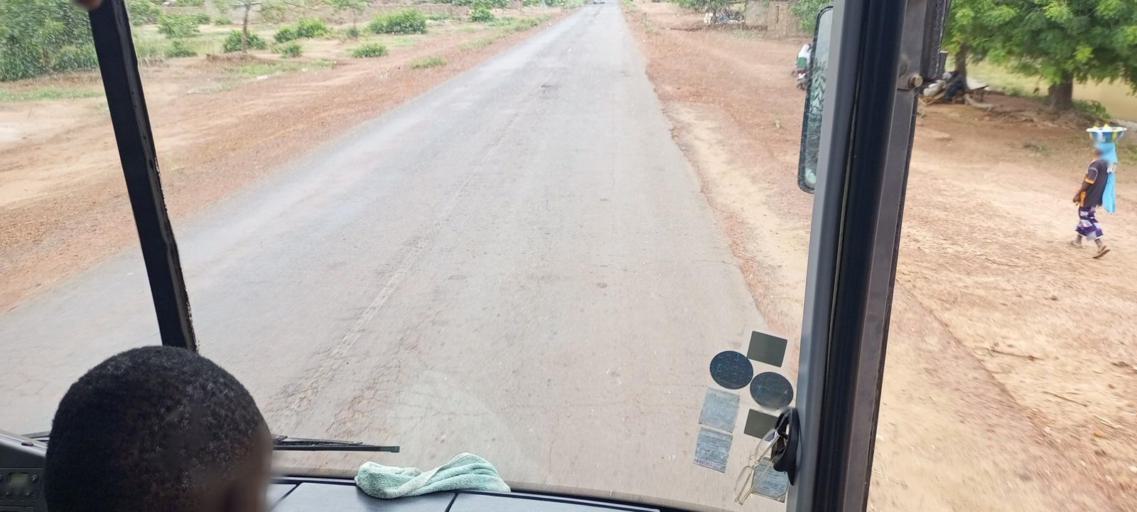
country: ML
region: Sikasso
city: Koutiala
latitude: 12.5778
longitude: -5.6085
